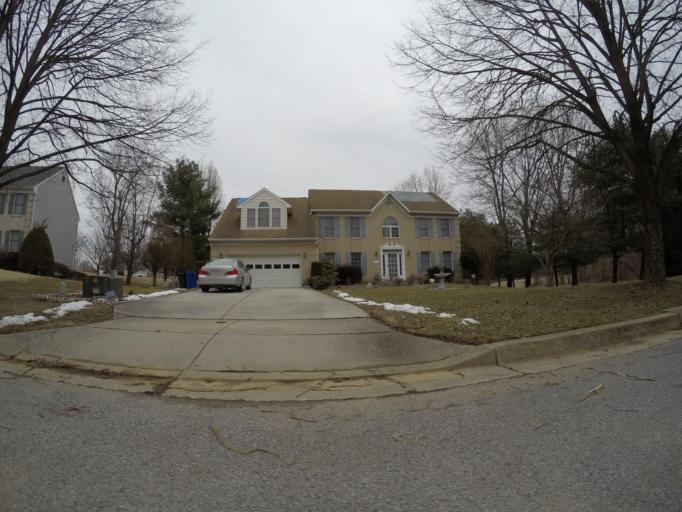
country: US
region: Maryland
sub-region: Howard County
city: Ellicott City
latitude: 39.2465
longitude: -76.8040
